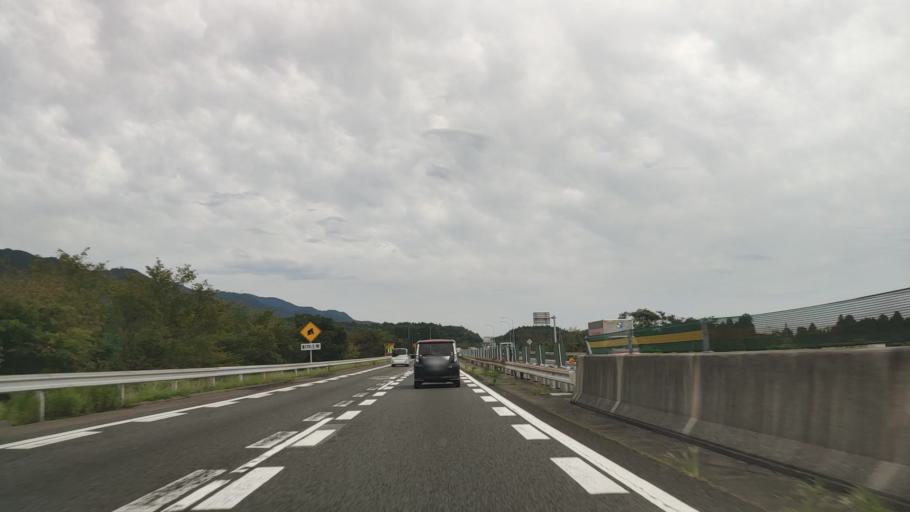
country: JP
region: Shiga Prefecture
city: Youkaichi
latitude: 35.1567
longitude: 136.2794
